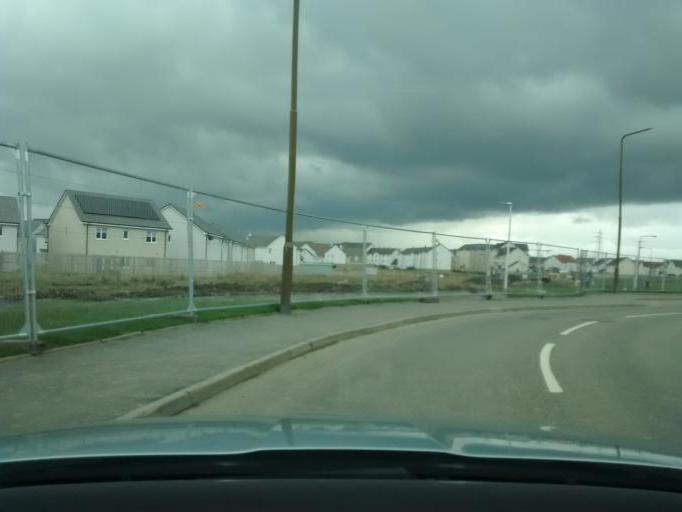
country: GB
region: Scotland
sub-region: West Lothian
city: Bathgate
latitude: 55.8893
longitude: -3.6440
